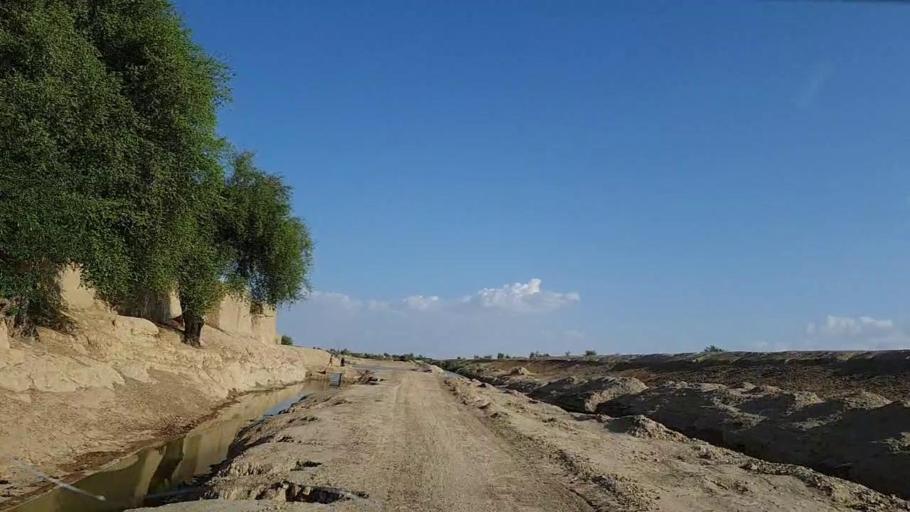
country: PK
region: Sindh
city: Johi
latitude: 26.5843
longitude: 67.5422
